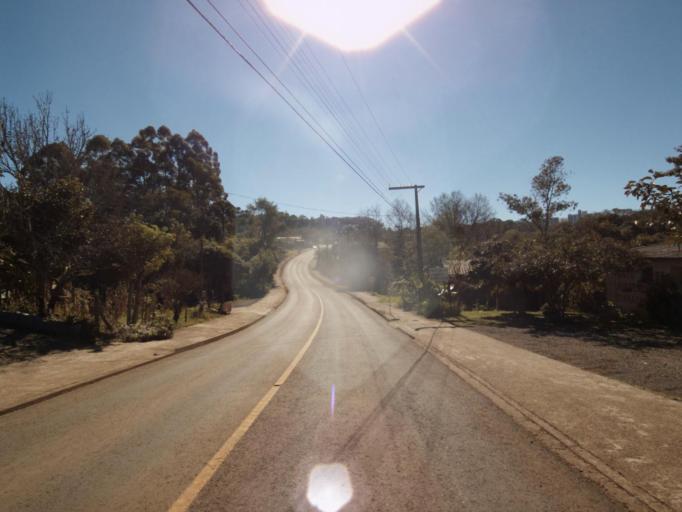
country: AR
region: Misiones
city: Bernardo de Irigoyen
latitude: -26.7148
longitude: -53.5252
